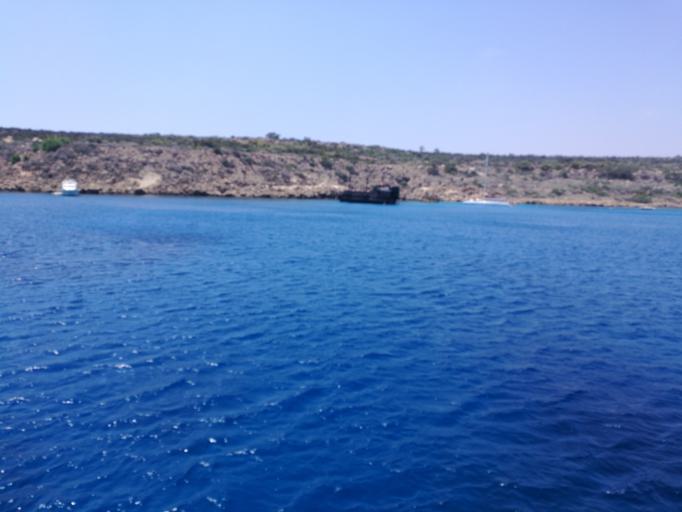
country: CY
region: Ammochostos
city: Protaras
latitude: 34.9781
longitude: 34.0755
